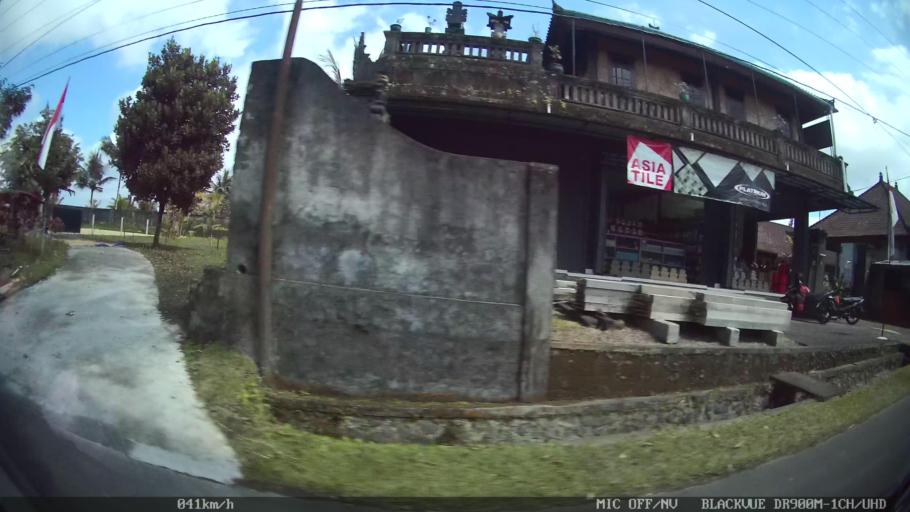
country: ID
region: Bali
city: Banjar Abuan
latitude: -8.4589
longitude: 115.3217
